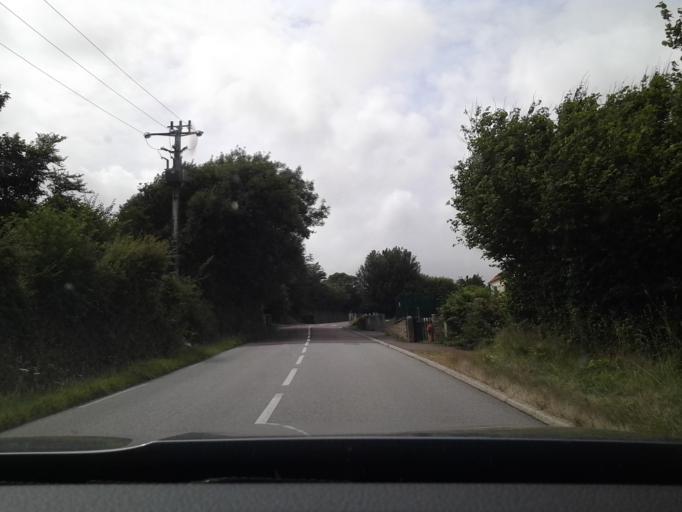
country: FR
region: Lower Normandy
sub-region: Departement de la Manche
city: Beaumont-Hague
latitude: 49.6736
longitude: -1.7909
